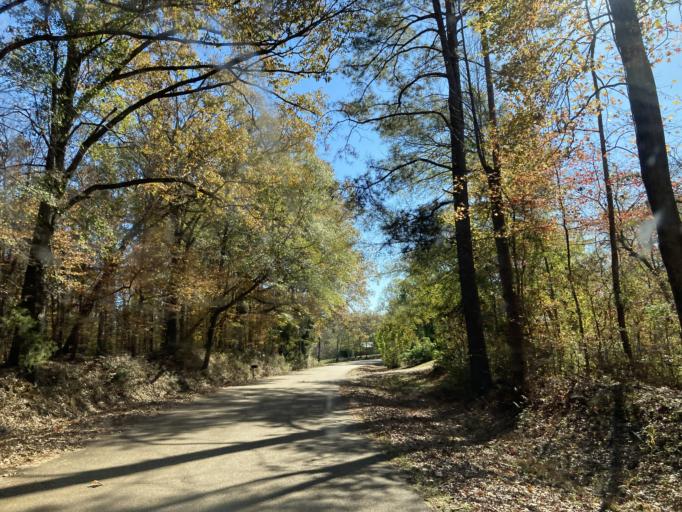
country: US
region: Mississippi
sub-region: Hinds County
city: Lynchburg
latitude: 32.5895
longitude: -90.5220
